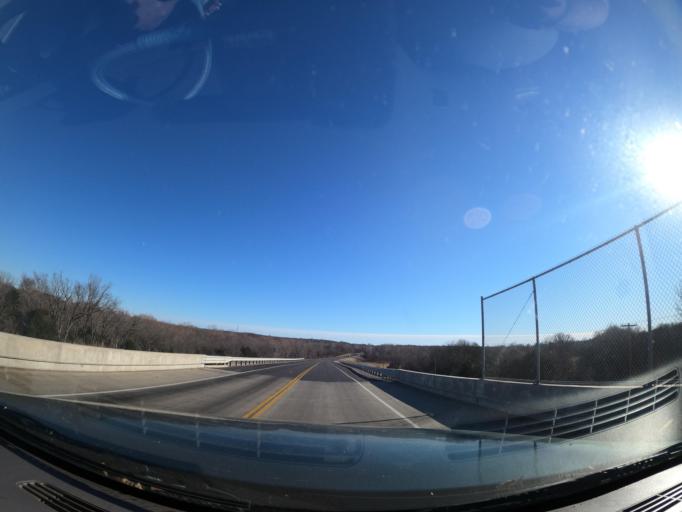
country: US
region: Oklahoma
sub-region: McIntosh County
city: Eufaula
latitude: 35.2680
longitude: -95.5833
